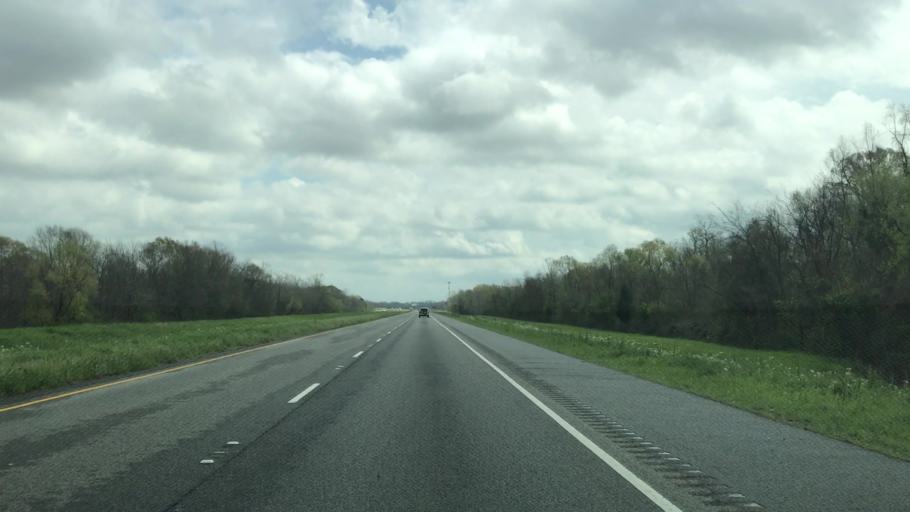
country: US
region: Louisiana
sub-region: Rapides Parish
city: Alexandria
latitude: 31.3558
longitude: -92.5550
